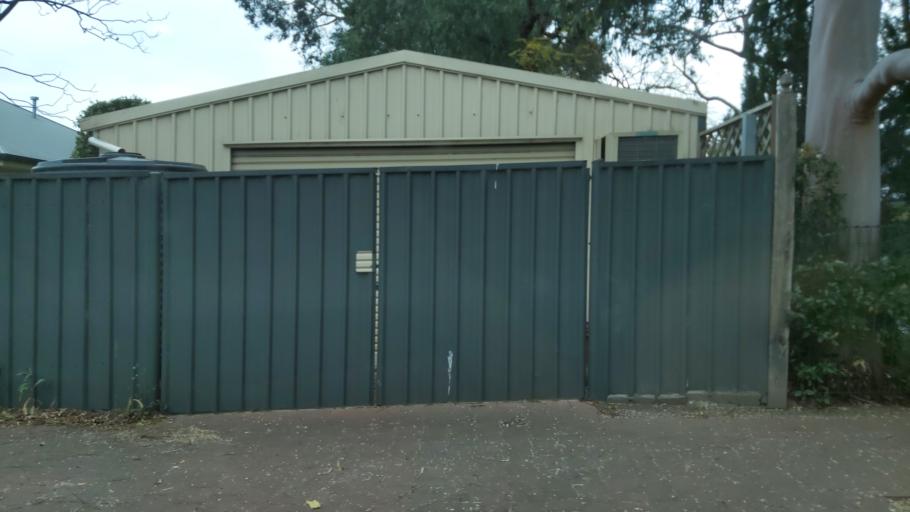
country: AU
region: South Australia
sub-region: Burnside
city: Glenunga
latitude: -34.9590
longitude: 138.6362
